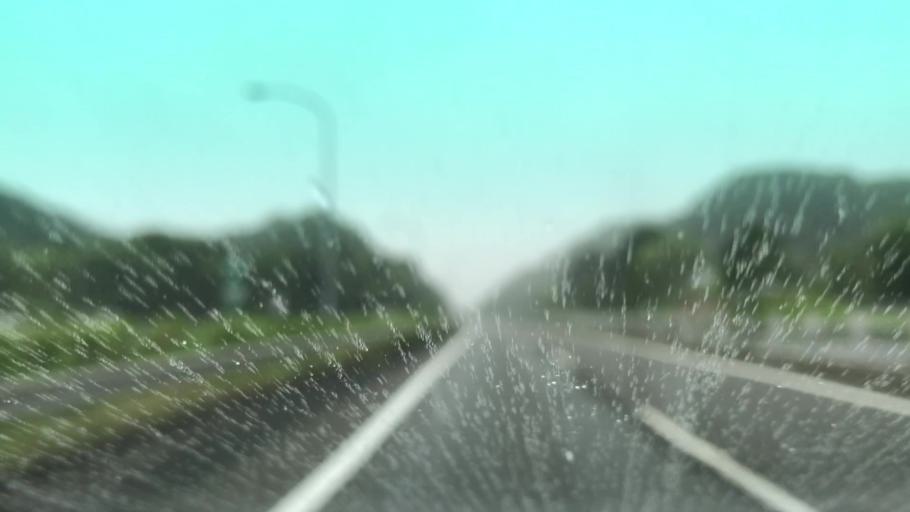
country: JP
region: Hokkaido
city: Shiraoi
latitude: 42.5432
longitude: 141.2854
